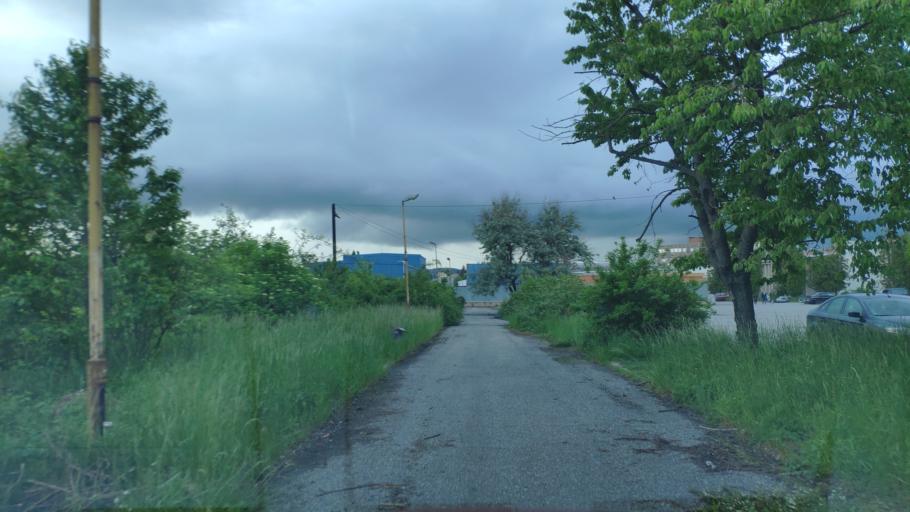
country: SK
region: Kosicky
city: Kosice
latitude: 48.7006
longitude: 21.2468
